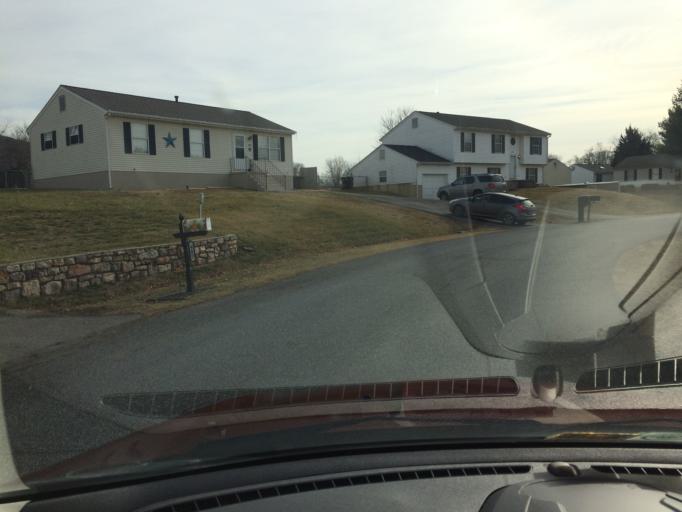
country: US
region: Virginia
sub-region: Roanoke County
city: Hollins
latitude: 37.3293
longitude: -79.9341
